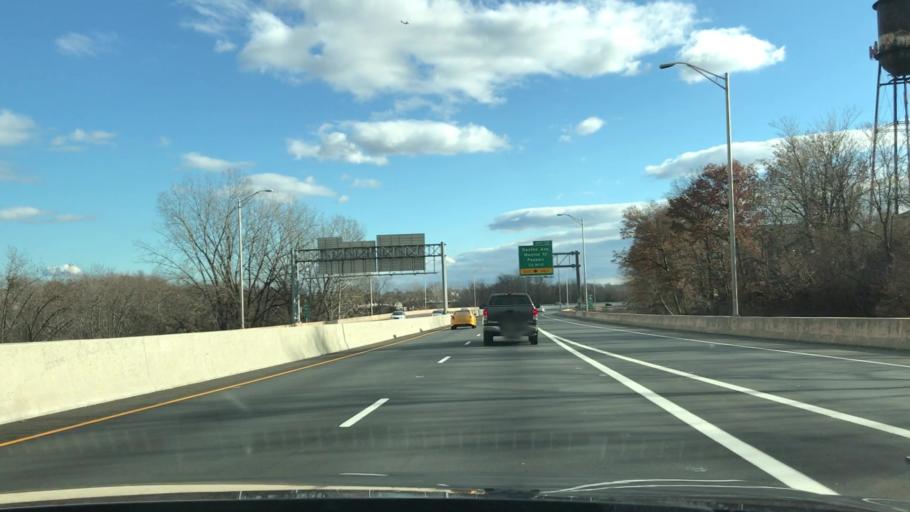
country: US
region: New Jersey
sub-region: Bergen County
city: Garfield
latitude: 40.8771
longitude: -74.1199
